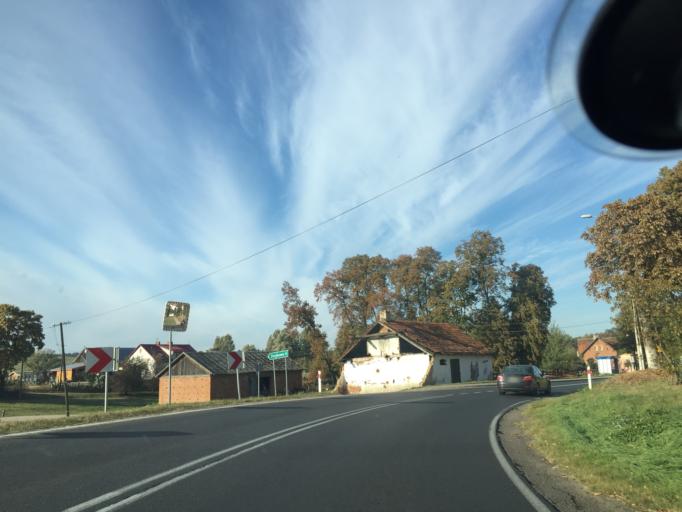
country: PL
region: Warmian-Masurian Voivodeship
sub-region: Powiat lidzbarski
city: Lidzbark Warminski
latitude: 54.0743
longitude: 20.5175
